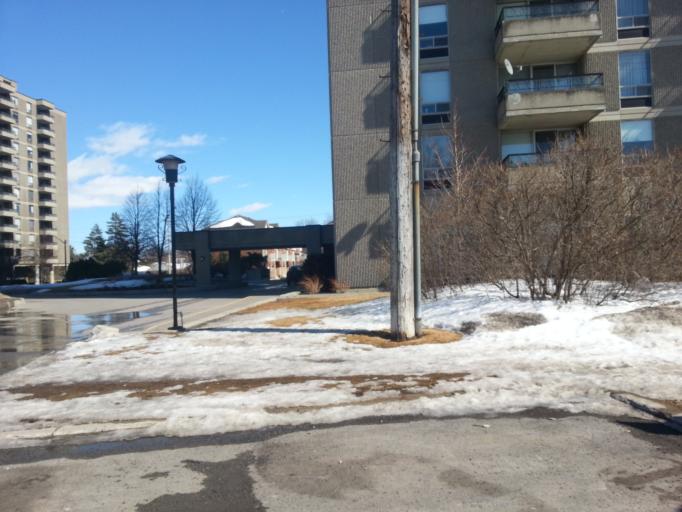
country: CA
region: Ontario
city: Ottawa
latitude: 45.3995
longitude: -75.7518
